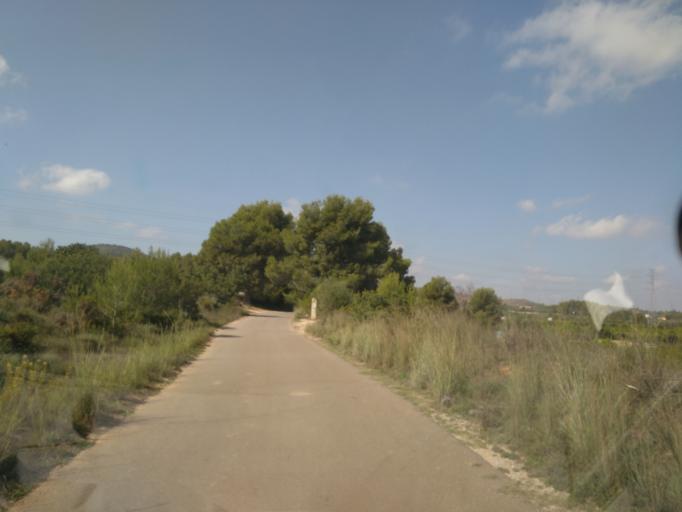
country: ES
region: Valencia
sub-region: Provincia de Valencia
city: Tous
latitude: 39.1748
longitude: -0.5943
